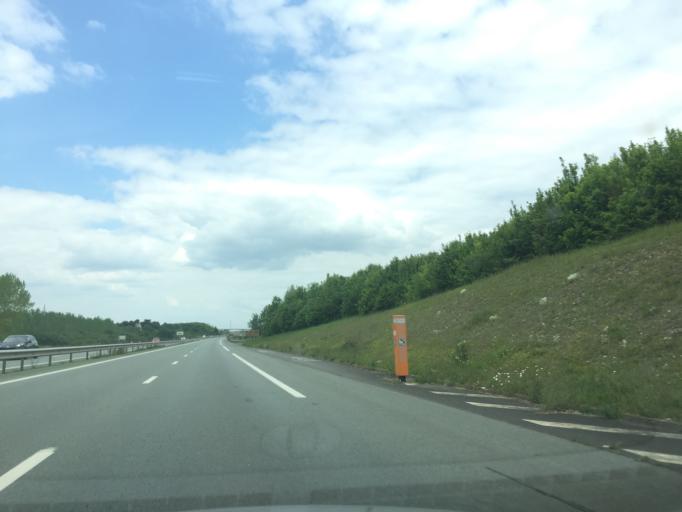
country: FR
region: Poitou-Charentes
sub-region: Departement des Deux-Sevres
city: Chauray
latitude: 46.3712
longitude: -0.3556
